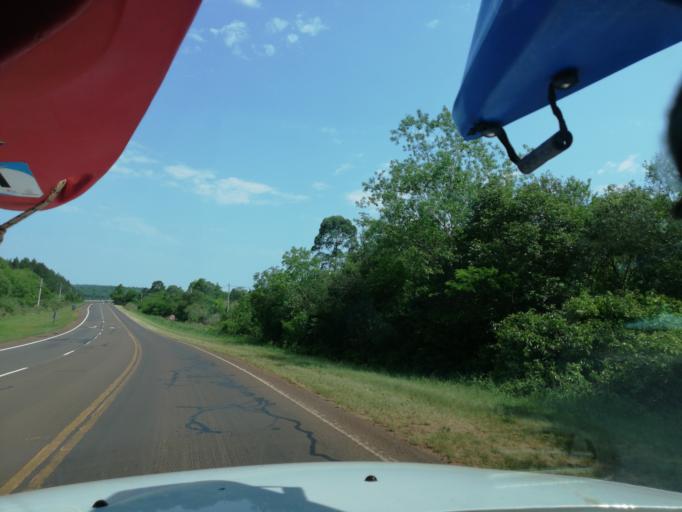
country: AR
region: Misiones
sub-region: Departamento de San Ignacio
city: San Ignacio
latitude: -27.2707
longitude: -55.5403
